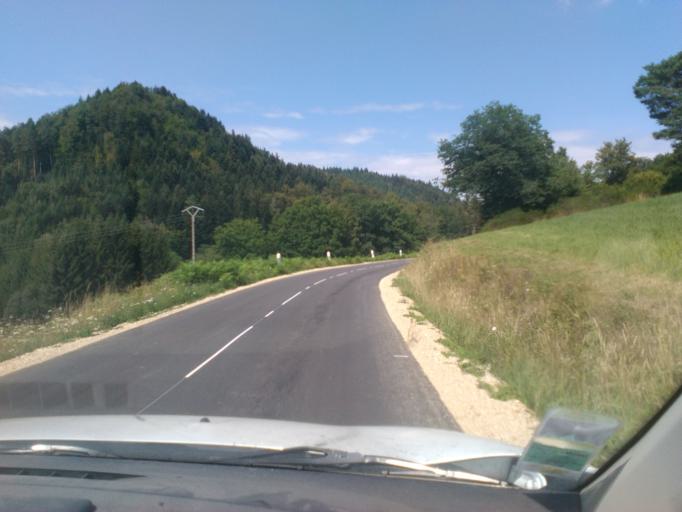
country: FR
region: Lorraine
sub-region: Departement des Vosges
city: Bruyeres
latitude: 48.1405
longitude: 6.6887
